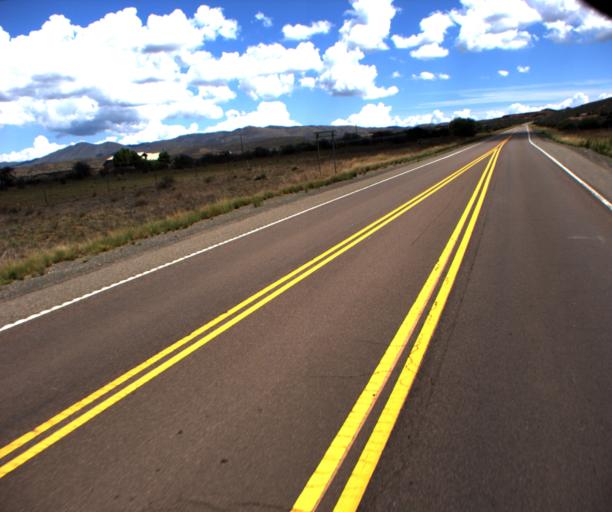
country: US
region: Arizona
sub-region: Yavapai County
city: Dewey-Humboldt
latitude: 34.5321
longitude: -112.2189
